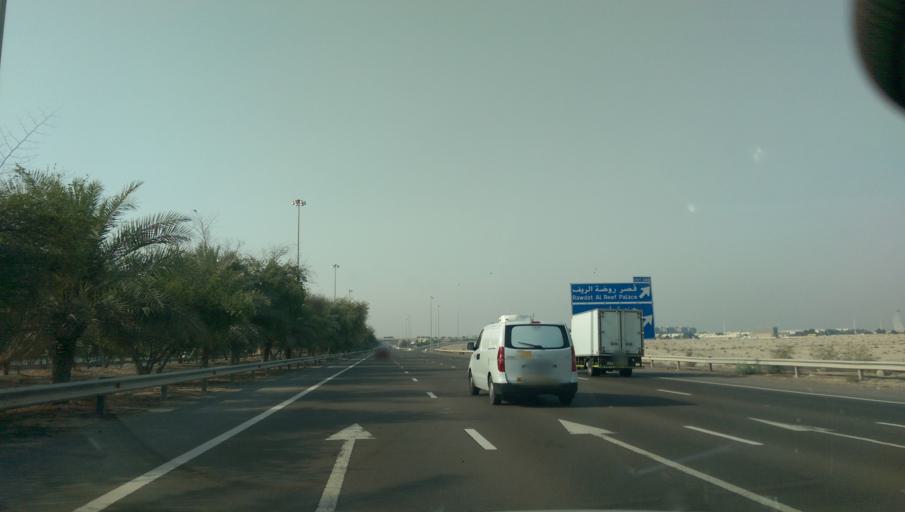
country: AE
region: Abu Dhabi
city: Abu Dhabi
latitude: 24.4703
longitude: 54.6764
